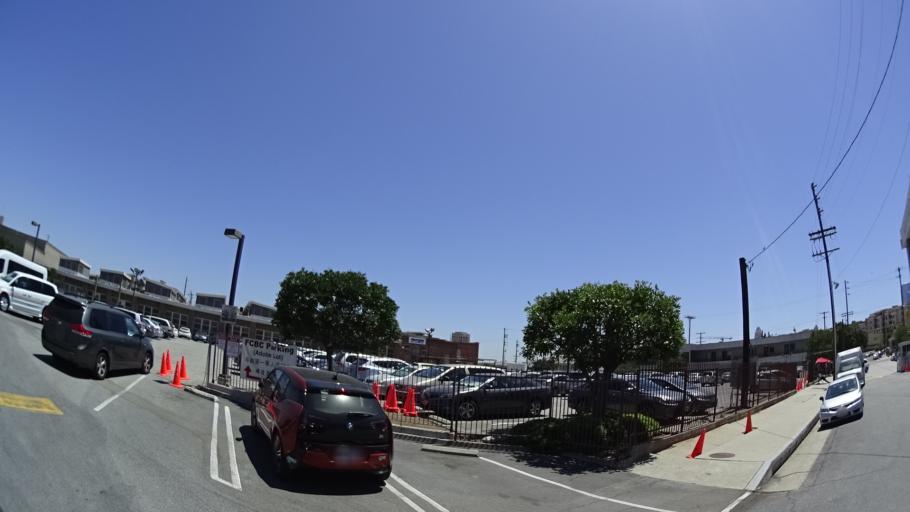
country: US
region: California
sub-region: Los Angeles County
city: Los Angeles
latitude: 34.0661
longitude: -118.2407
